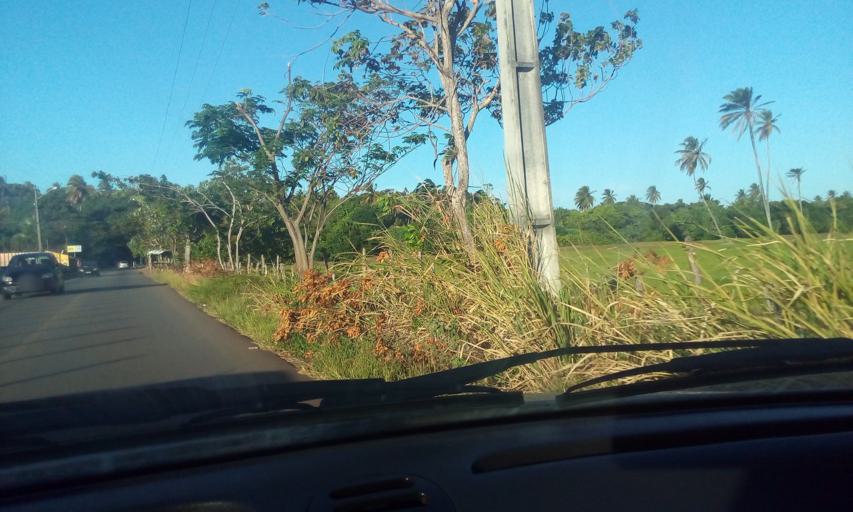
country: BR
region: Rio Grande do Norte
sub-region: Parnamirim
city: Parnamirim
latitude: -5.9548
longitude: -35.1628
